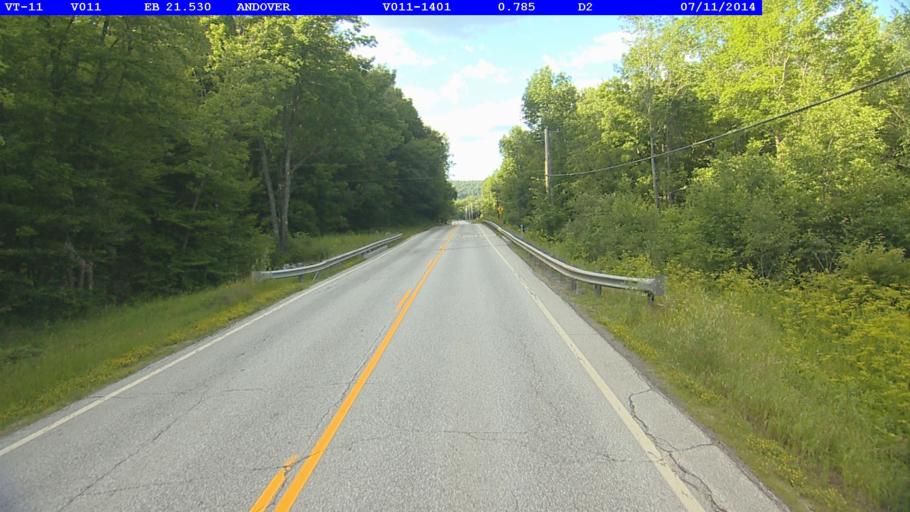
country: US
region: Vermont
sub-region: Windsor County
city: Chester
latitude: 43.2436
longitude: -72.7234
